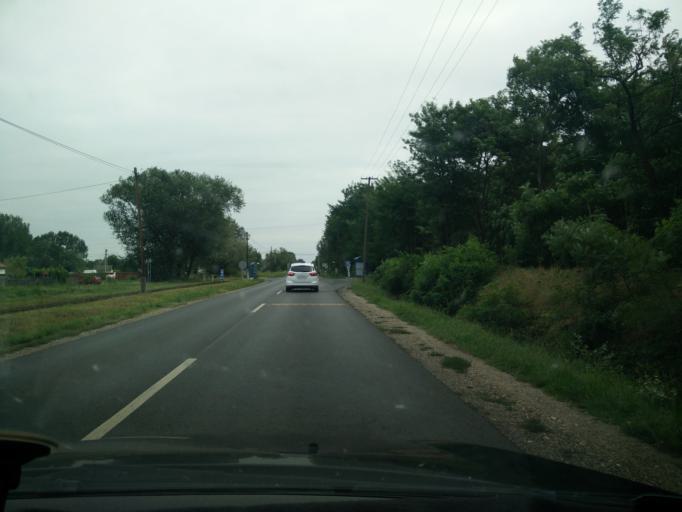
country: HU
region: Hajdu-Bihar
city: Debrecen
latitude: 47.5312
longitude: 21.7024
